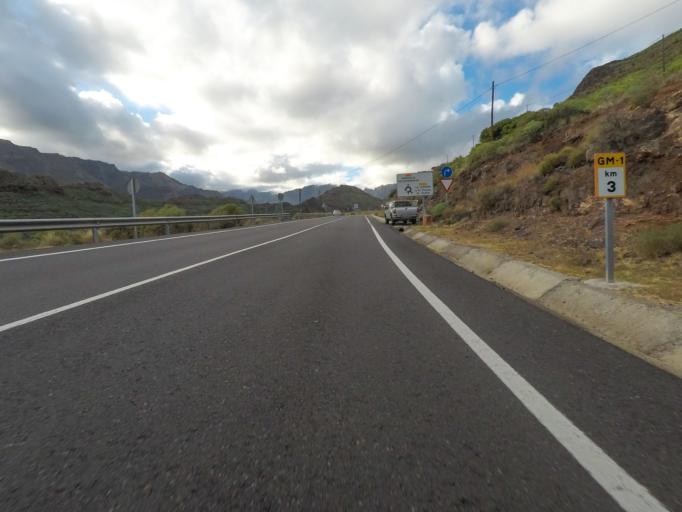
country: ES
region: Canary Islands
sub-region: Provincia de Santa Cruz de Tenerife
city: San Sebastian de la Gomera
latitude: 28.1105
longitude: -17.1289
